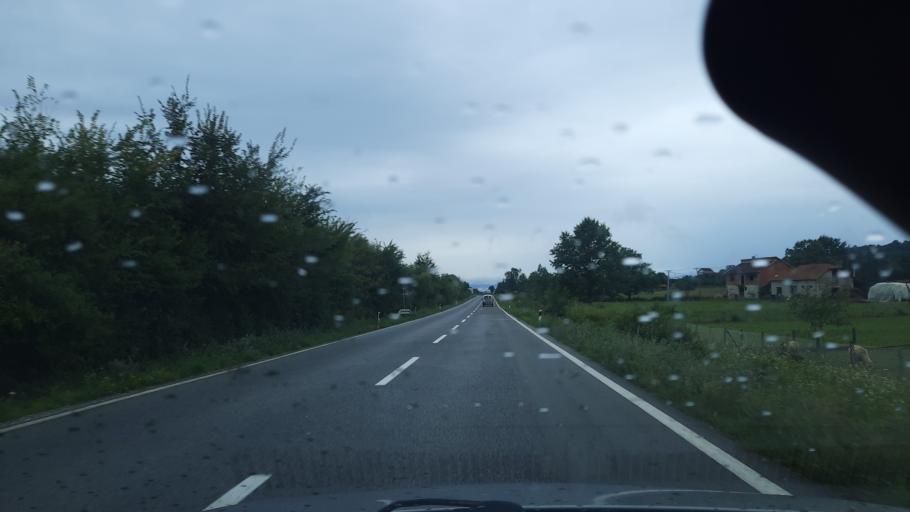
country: RS
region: Central Serbia
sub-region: Sumadijski Okrug
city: Knic
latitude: 43.8187
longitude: 20.7810
